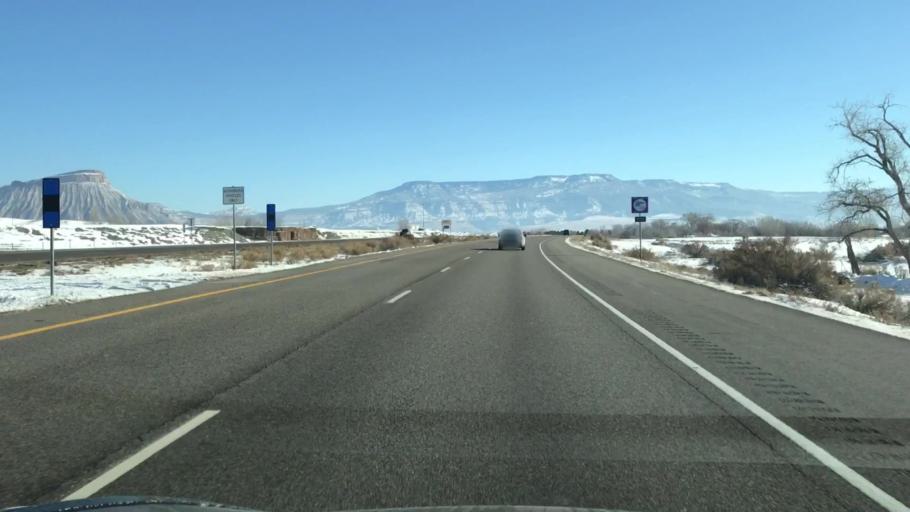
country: US
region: Colorado
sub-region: Mesa County
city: Fruitvale
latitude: 39.1074
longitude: -108.4964
